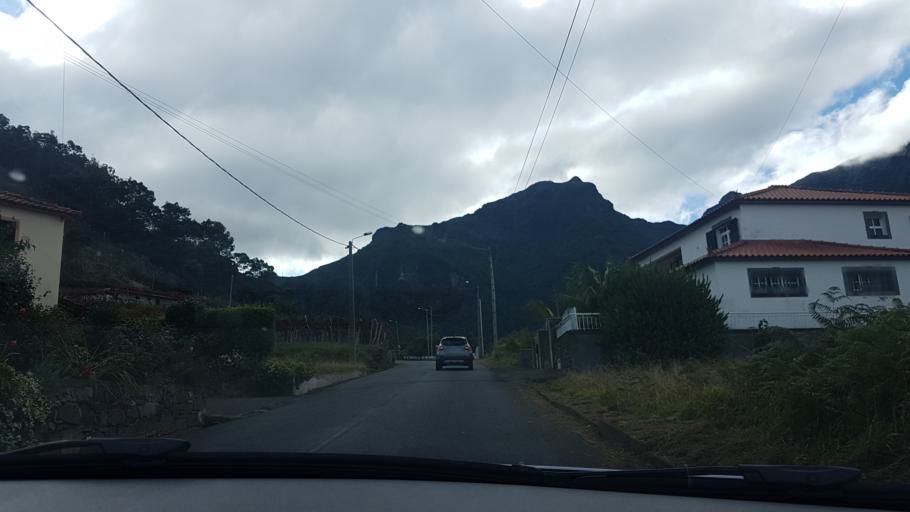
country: PT
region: Madeira
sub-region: Sao Vicente
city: Sao Vicente
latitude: 32.7787
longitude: -17.0293
